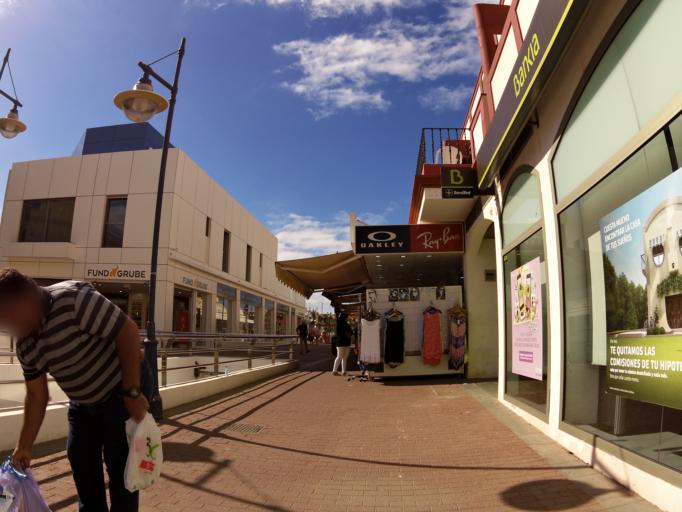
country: ES
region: Canary Islands
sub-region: Provincia de Las Palmas
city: Puerto Rico
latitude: 27.8191
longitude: -15.7639
